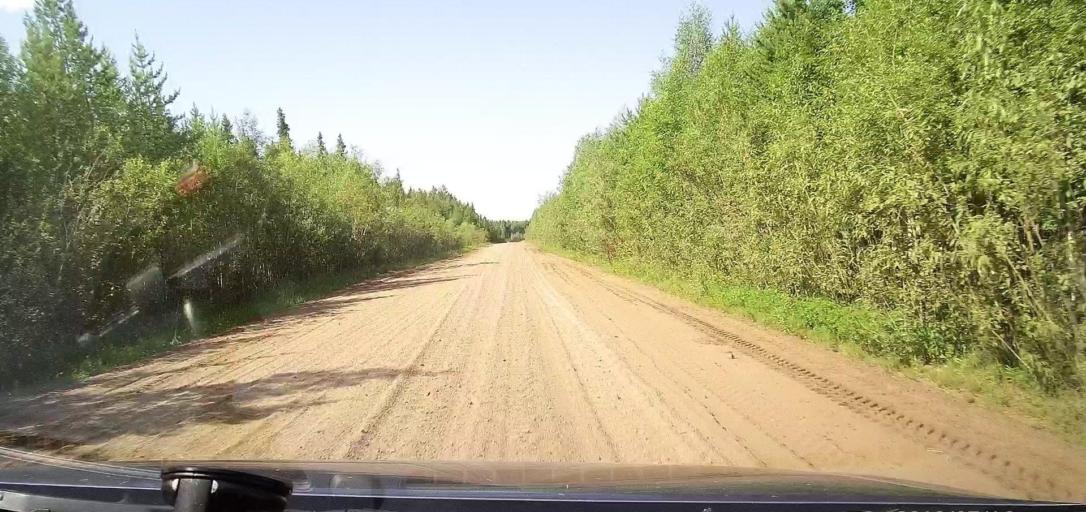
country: RU
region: Arkhangelskaya
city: Leshukonskoye
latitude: 65.4094
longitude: 45.0879
